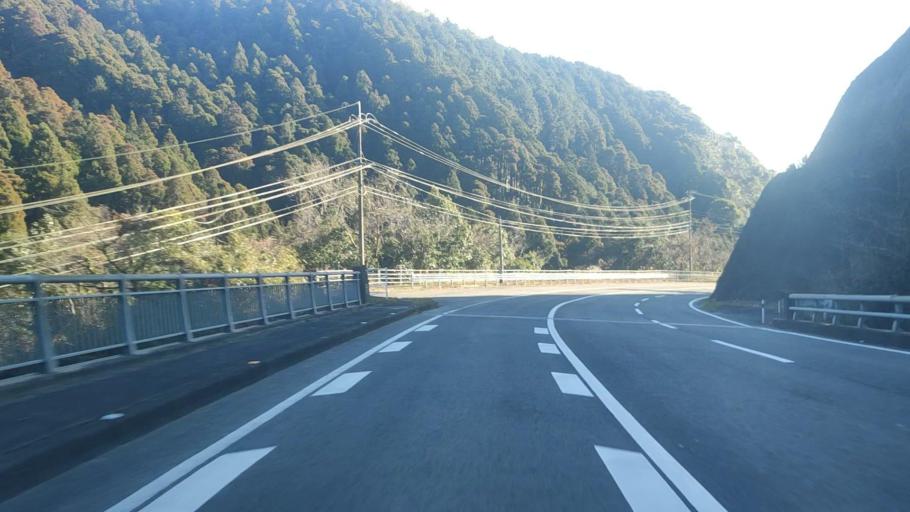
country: JP
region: Saga Prefecture
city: Kanzakimachi-kanzaki
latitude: 33.3859
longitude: 130.2606
